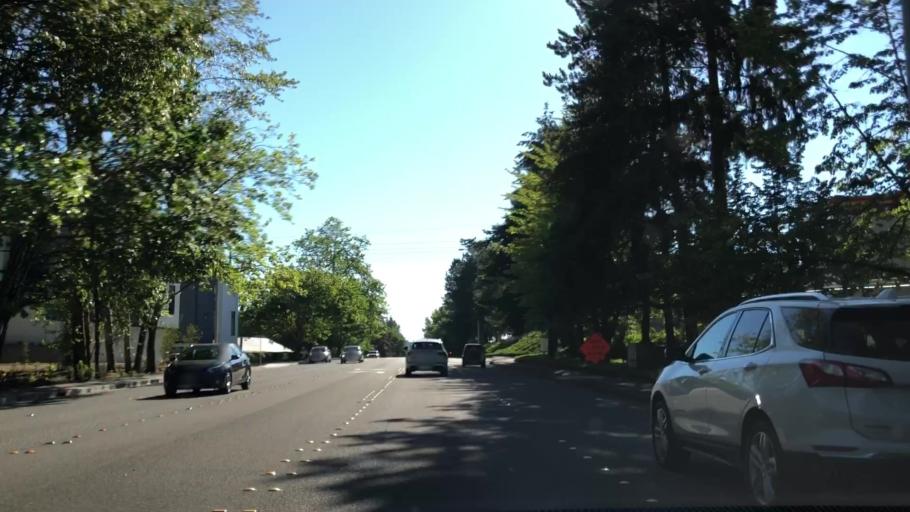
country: US
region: Washington
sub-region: King County
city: Bellevue
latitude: 47.6235
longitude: -122.1581
